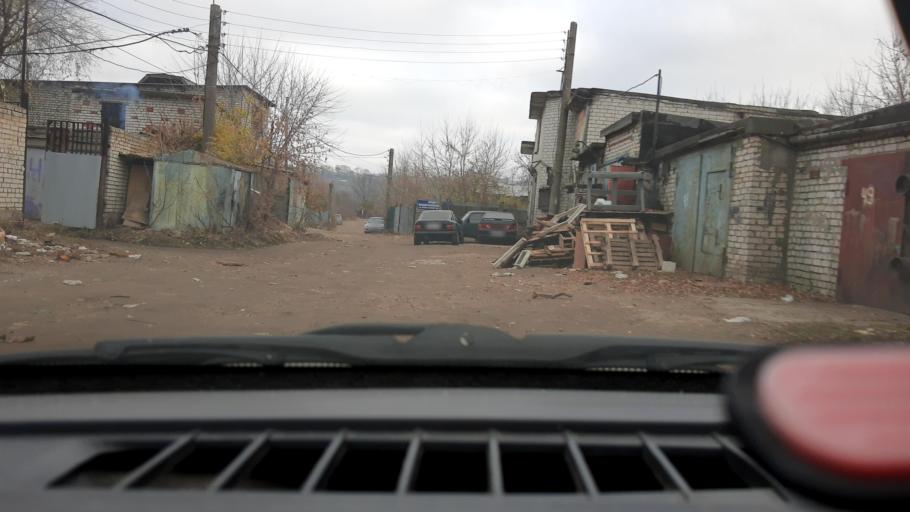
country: RU
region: Nizjnij Novgorod
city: Nizhniy Novgorod
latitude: 56.2614
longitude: 43.9450
